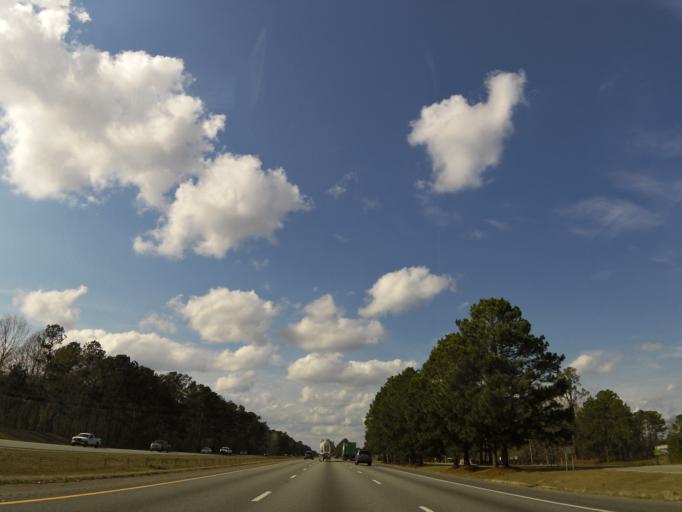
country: US
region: South Carolina
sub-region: Berkeley County
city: Ladson
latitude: 33.0091
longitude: -80.1086
